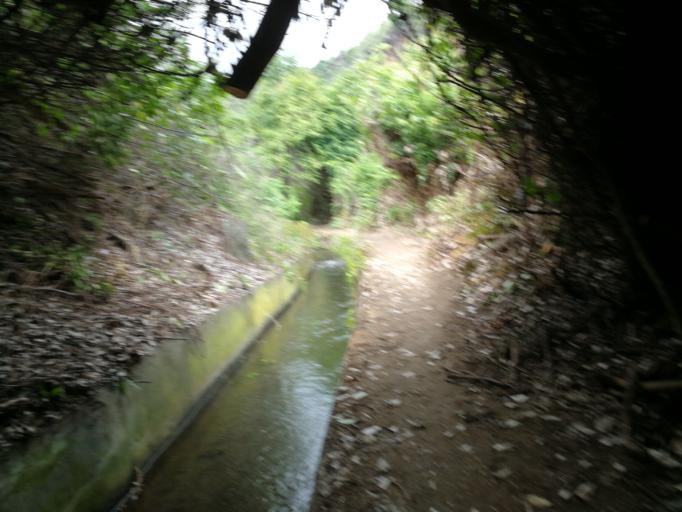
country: RE
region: Reunion
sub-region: Reunion
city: Saint-Paul
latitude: -21.0454
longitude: 55.2440
